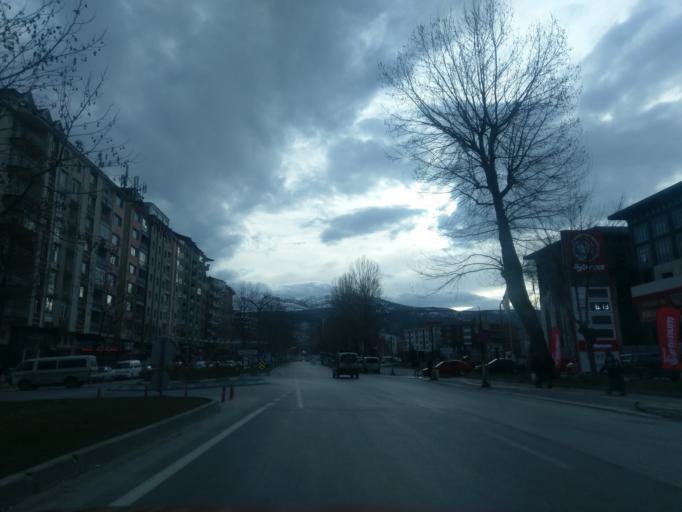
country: TR
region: Kuetahya
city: Kutahya
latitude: 39.4264
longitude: 29.9909
